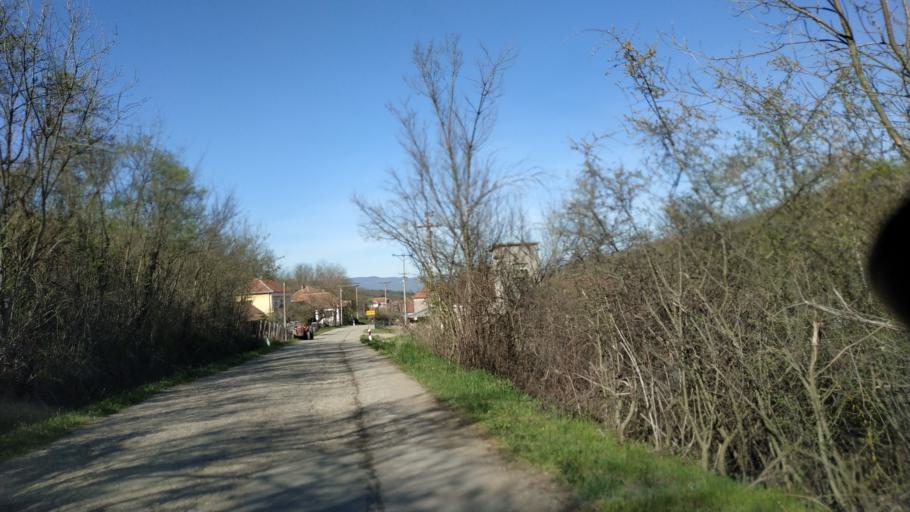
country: RS
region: Central Serbia
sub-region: Nisavski Okrug
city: Aleksinac
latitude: 43.4795
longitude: 21.6524
